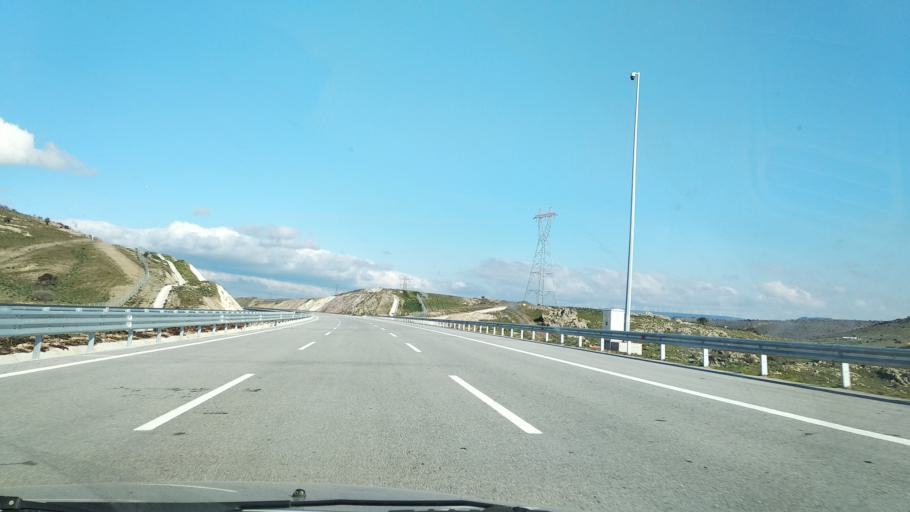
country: TR
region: Izmir
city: Yenisakran
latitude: 38.8328
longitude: 27.0432
